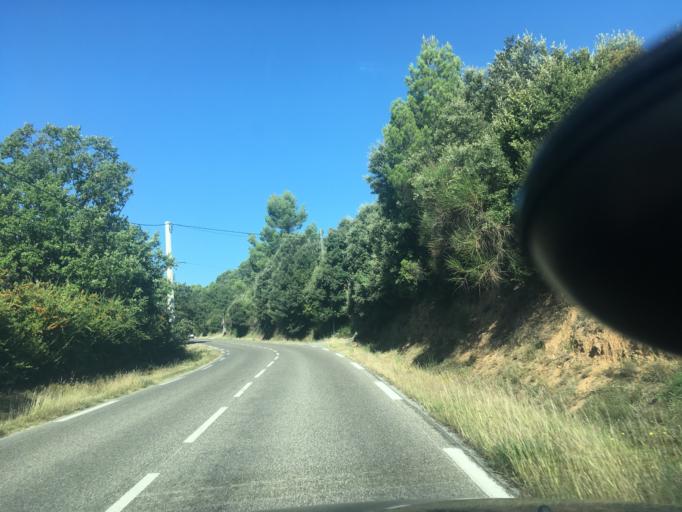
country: FR
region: Provence-Alpes-Cote d'Azur
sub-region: Departement du Var
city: Regusse
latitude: 43.6505
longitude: 6.1587
